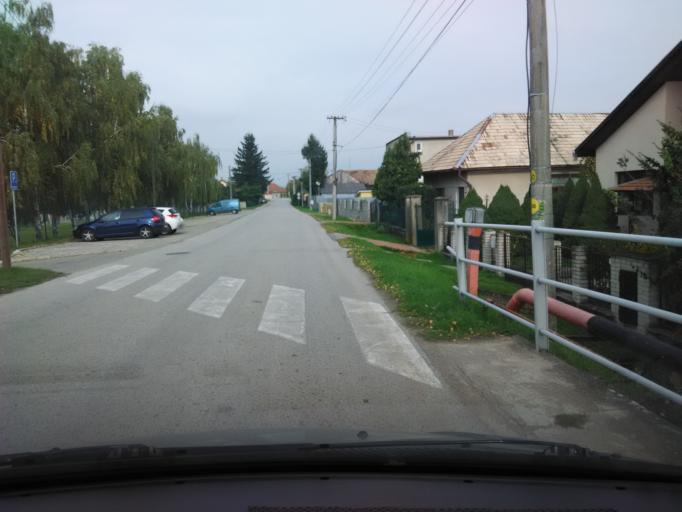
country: SK
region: Nitriansky
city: Tlmace
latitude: 48.2071
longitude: 18.5220
